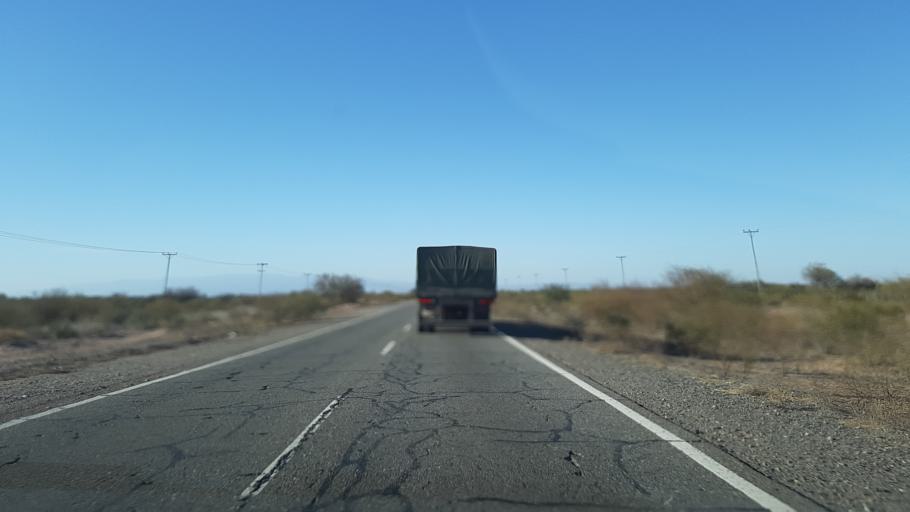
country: AR
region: San Juan
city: Caucete
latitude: -31.6493
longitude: -67.7636
